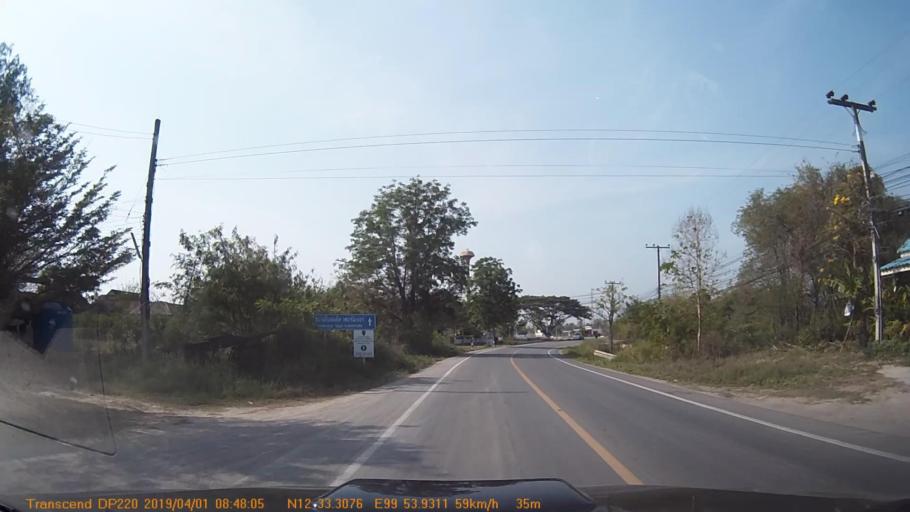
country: TH
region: Prachuap Khiri Khan
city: Hua Hin
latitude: 12.5549
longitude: 99.8989
